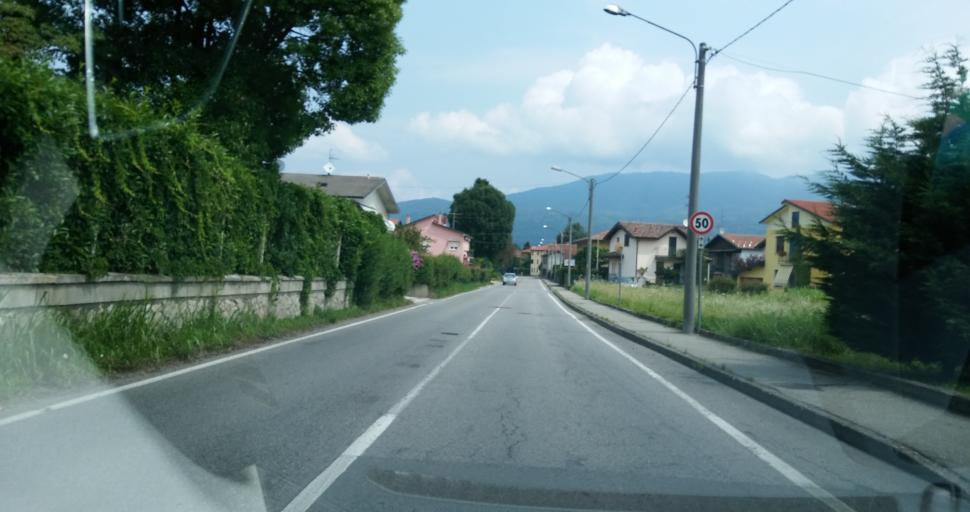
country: IT
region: Lombardy
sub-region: Provincia di Varese
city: Biandronno
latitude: 45.8137
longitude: 8.7105
